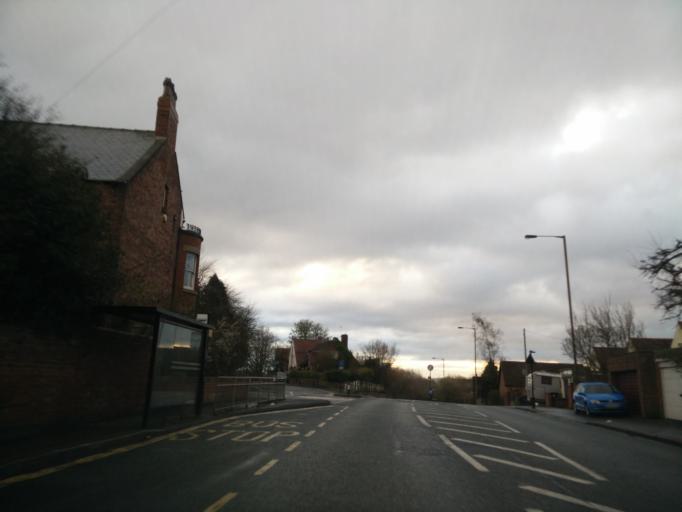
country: GB
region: England
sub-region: County Durham
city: Durham
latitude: 54.7724
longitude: -1.5924
